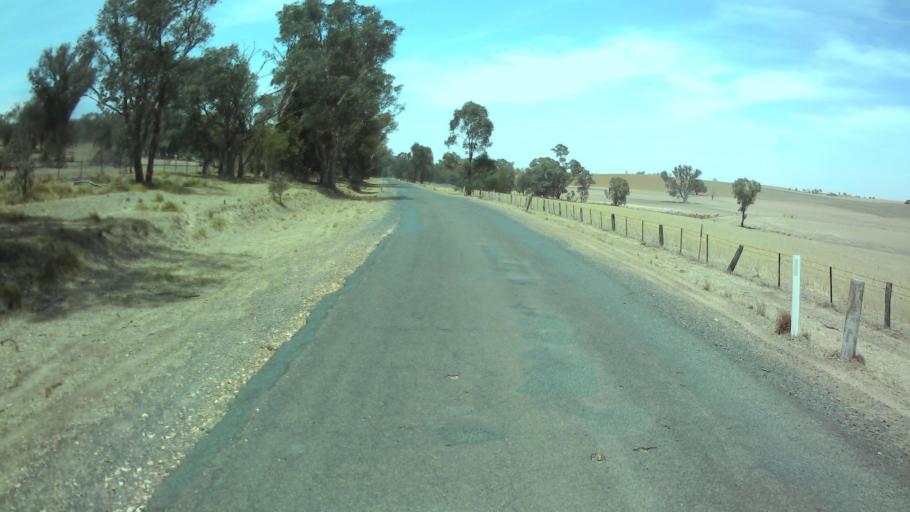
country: AU
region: New South Wales
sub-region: Weddin
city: Grenfell
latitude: -34.0228
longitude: 148.4323
